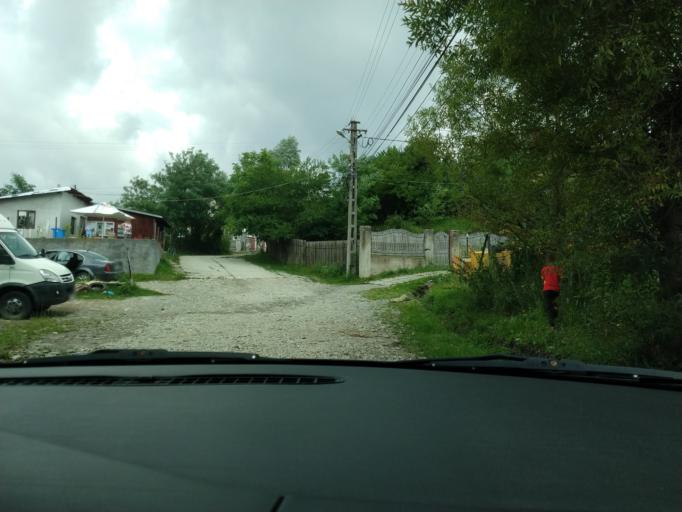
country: RO
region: Prahova
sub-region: Oras Breaza
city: Valea Tarsei
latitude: 45.1849
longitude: 25.6302
